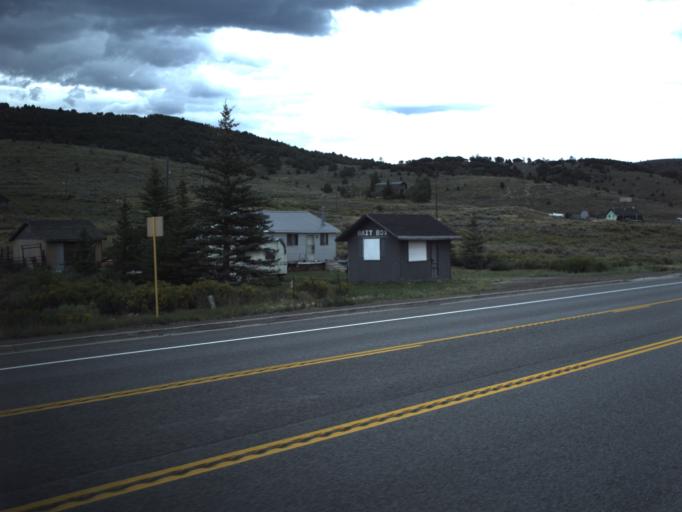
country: US
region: Utah
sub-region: Carbon County
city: Helper
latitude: 39.9284
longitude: -111.0827
